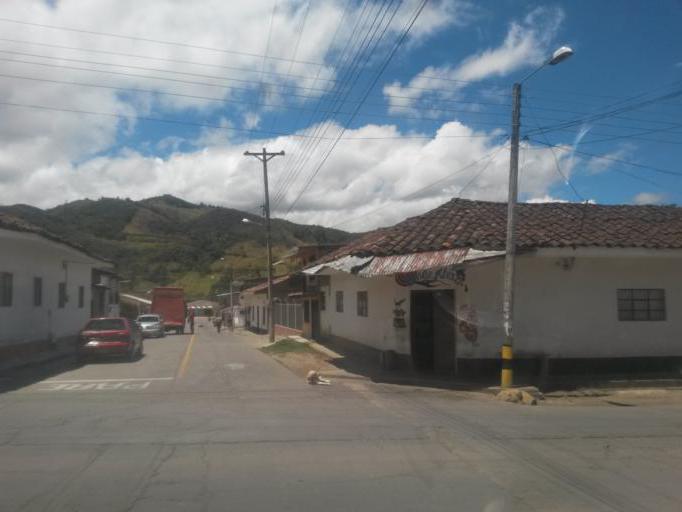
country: CO
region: Cauca
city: Silvia
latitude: 2.6102
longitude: -76.3828
